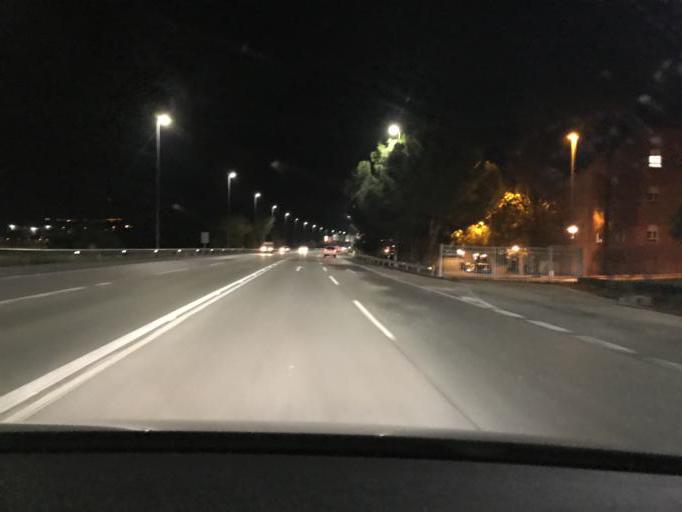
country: ES
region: Andalusia
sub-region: Provincia de Jaen
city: Jaen
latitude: 37.7902
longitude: -3.7780
